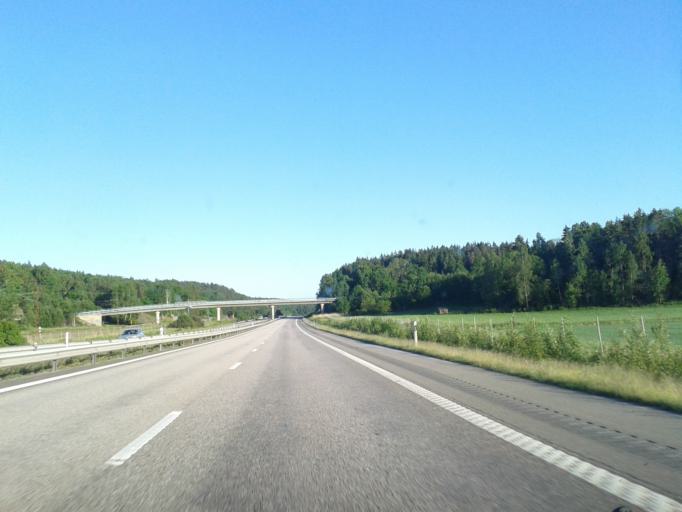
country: SE
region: Vaestra Goetaland
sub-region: Uddevalla Kommun
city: Ljungskile
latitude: 58.2775
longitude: 11.8848
